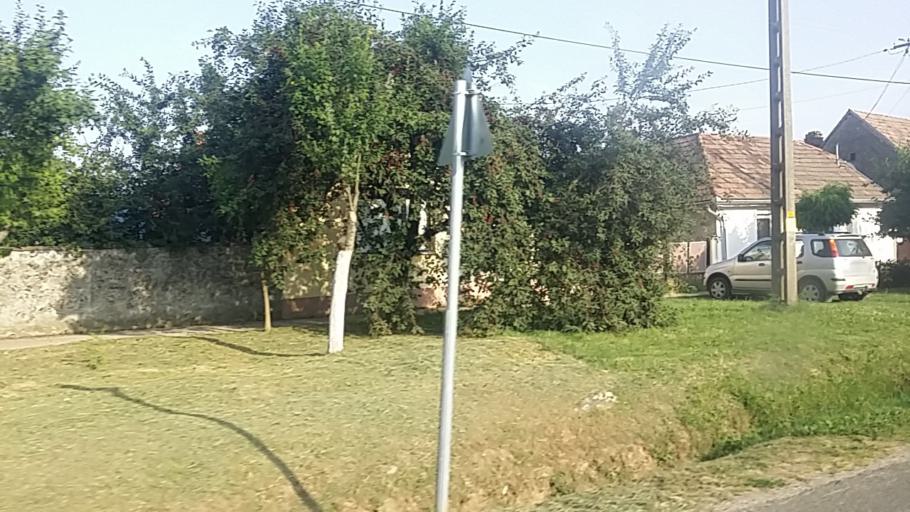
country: HU
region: Baranya
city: Siklos
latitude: 45.8583
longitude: 18.3637
